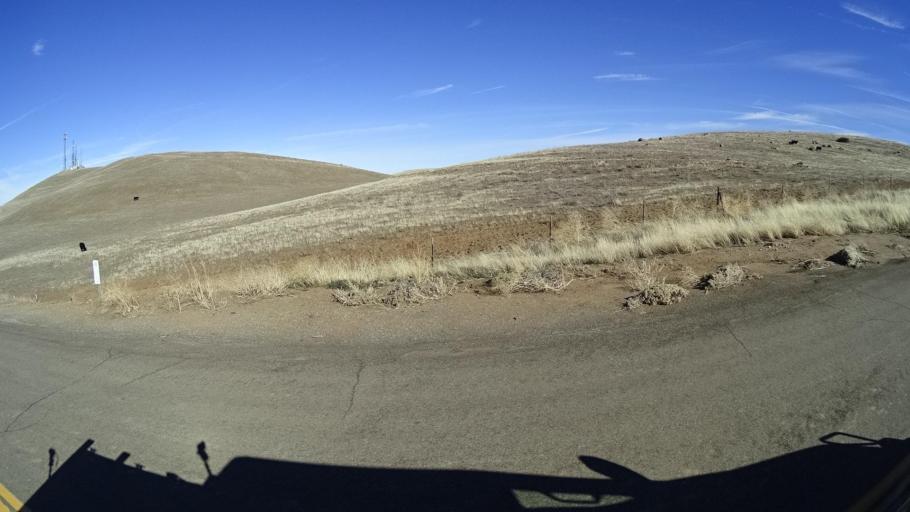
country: US
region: California
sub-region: Kern County
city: Maricopa
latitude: 34.9154
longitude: -119.4037
